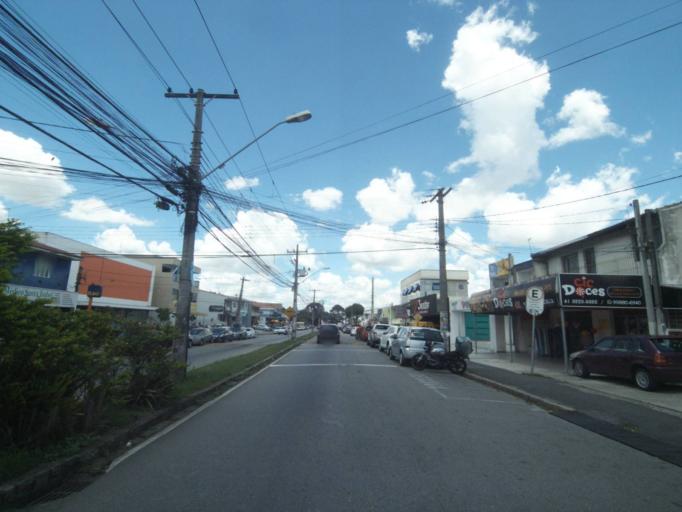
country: BR
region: Parana
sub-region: Curitiba
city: Curitiba
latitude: -25.5095
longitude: -49.3229
